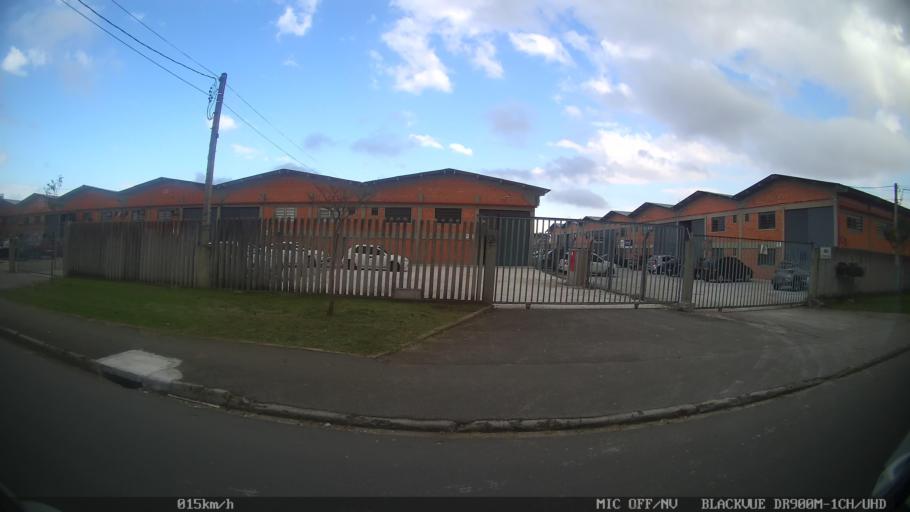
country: BR
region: Parana
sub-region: Pinhais
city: Pinhais
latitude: -25.4372
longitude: -49.1970
